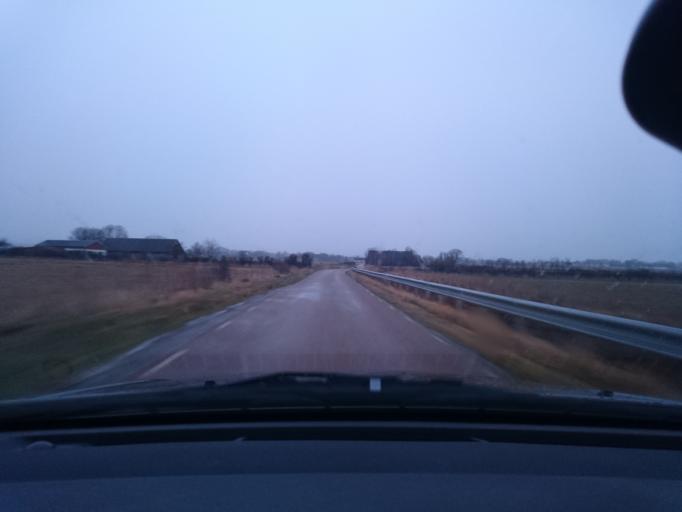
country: SE
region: Skane
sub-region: Angelholms Kommun
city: Vejbystrand
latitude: 56.3439
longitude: 12.7631
